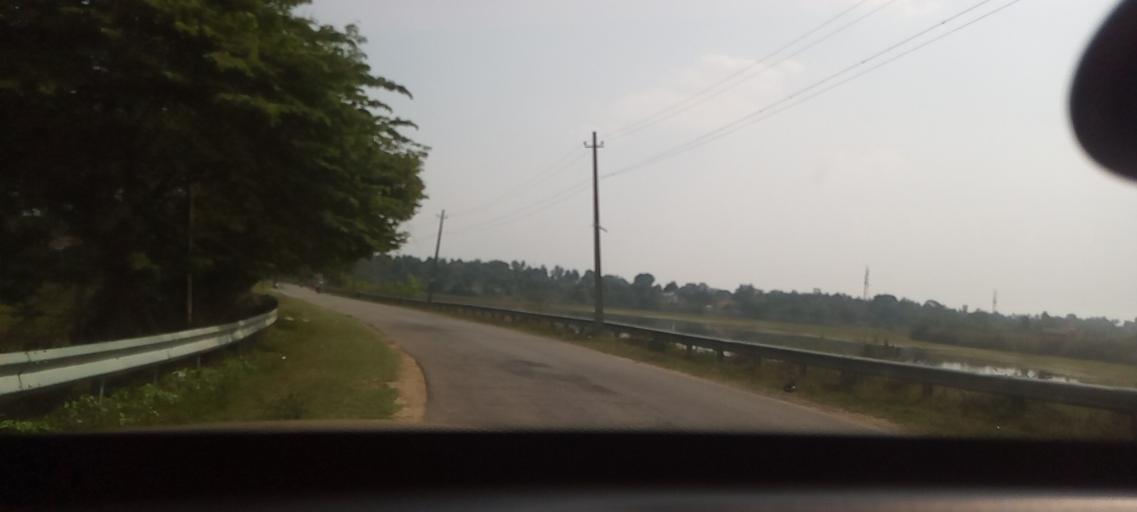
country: IN
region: Karnataka
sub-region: Hassan
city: Belur
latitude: 13.1714
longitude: 75.8597
